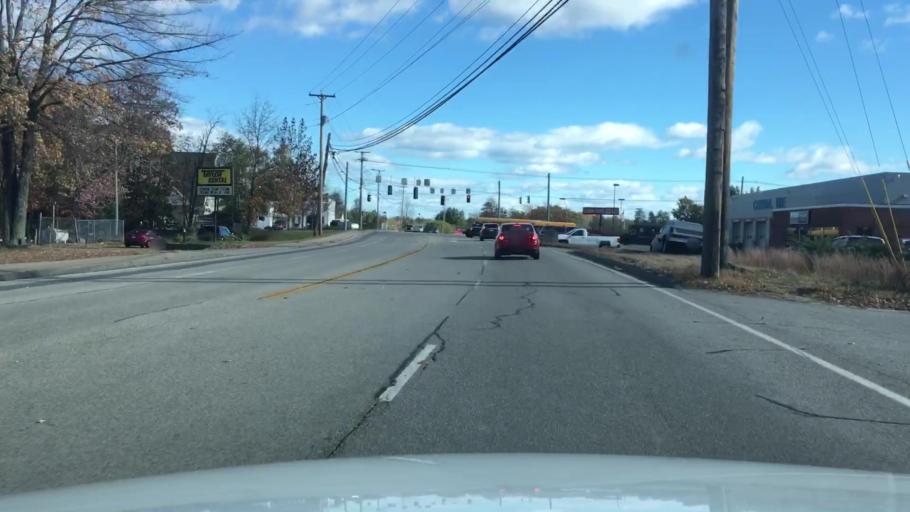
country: US
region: Maine
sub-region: York County
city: South Sanford
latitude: 43.4165
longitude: -70.7525
